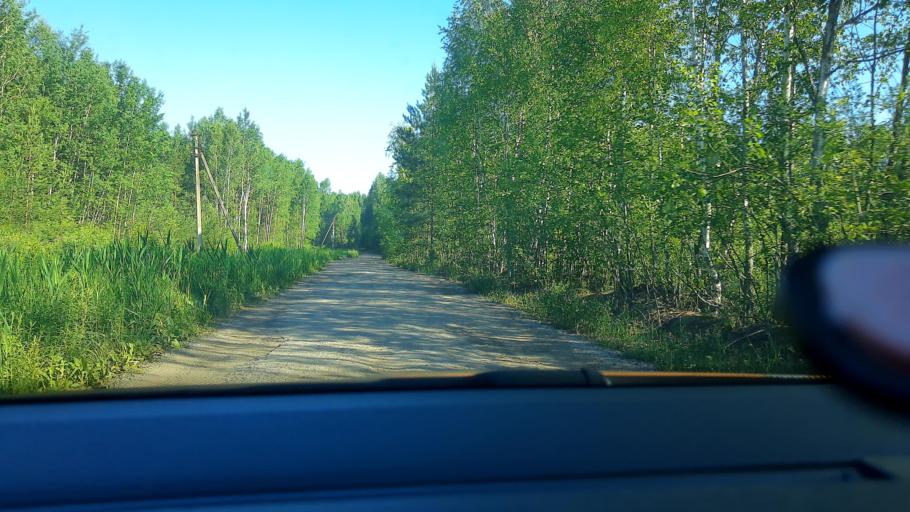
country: RU
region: Moskovskaya
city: Elektrogorsk
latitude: 55.8955
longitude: 38.7163
